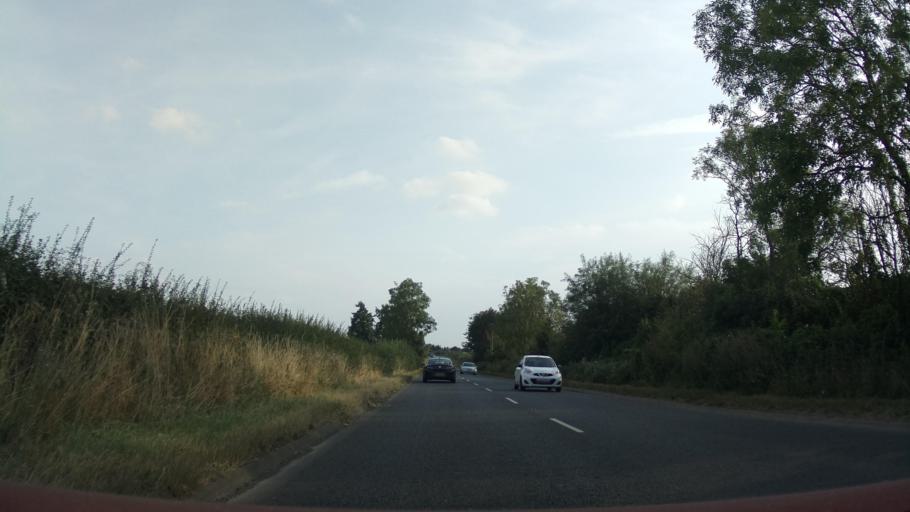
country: GB
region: England
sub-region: Gloucestershire
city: Gotherington
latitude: 51.9696
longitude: -2.0705
